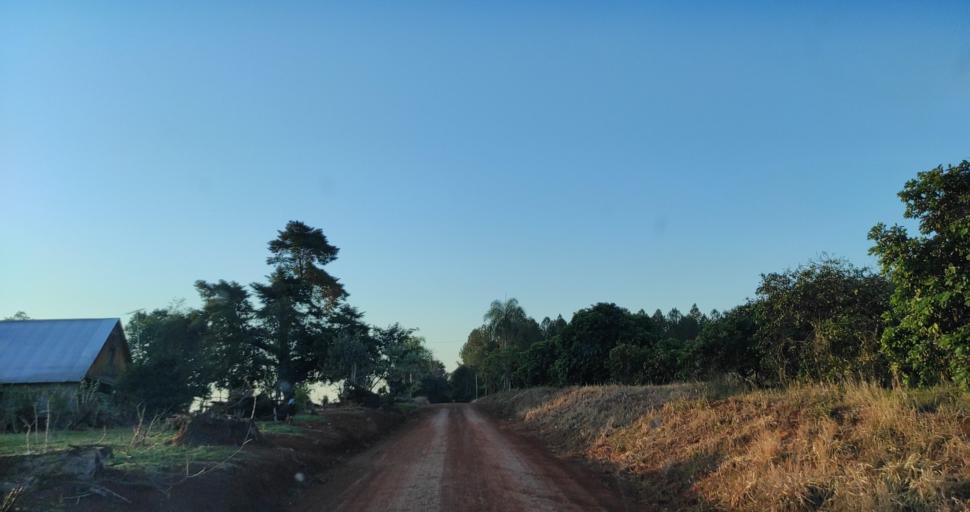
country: AR
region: Misiones
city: Capiovi
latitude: -26.8760
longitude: -55.1078
